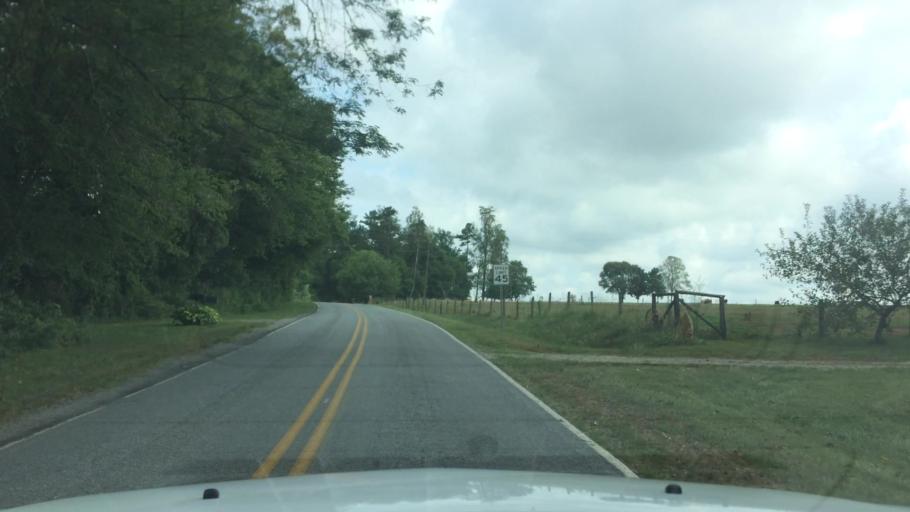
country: US
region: North Carolina
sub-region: Yadkin County
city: Jonesville
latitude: 36.1107
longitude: -80.8564
